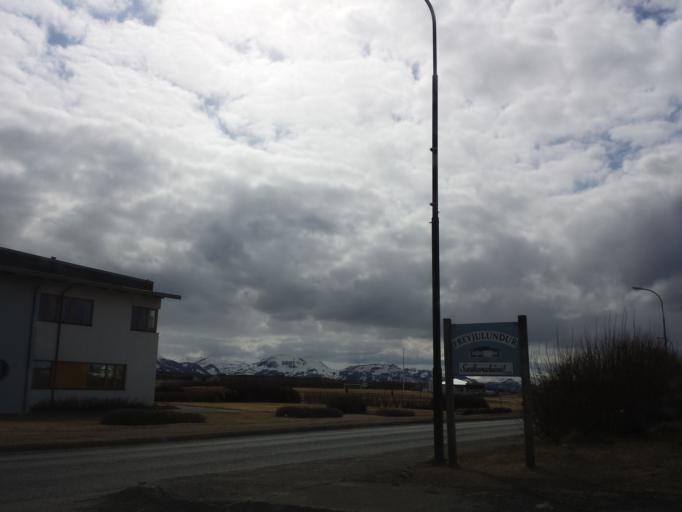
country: IS
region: West
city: Stykkisholmur
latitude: 65.0738
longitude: -22.7309
